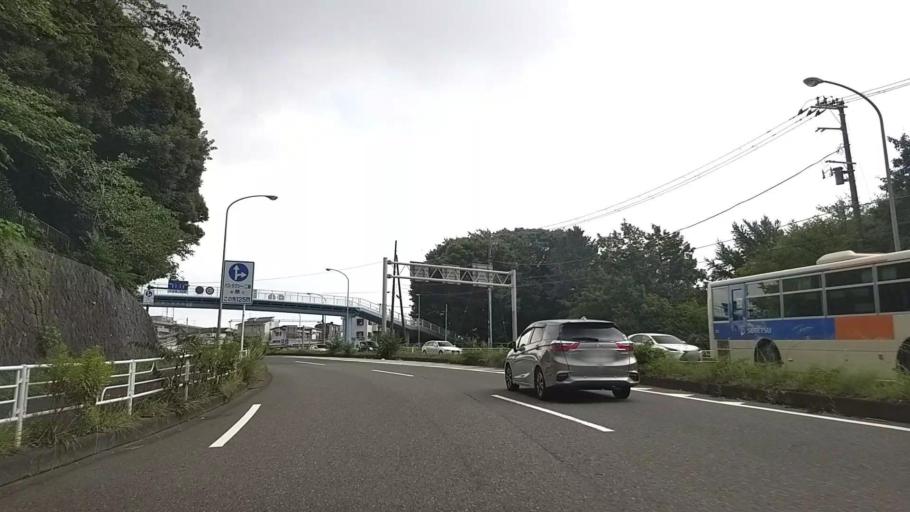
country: JP
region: Kanagawa
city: Yokohama
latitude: 35.4709
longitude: 139.6054
